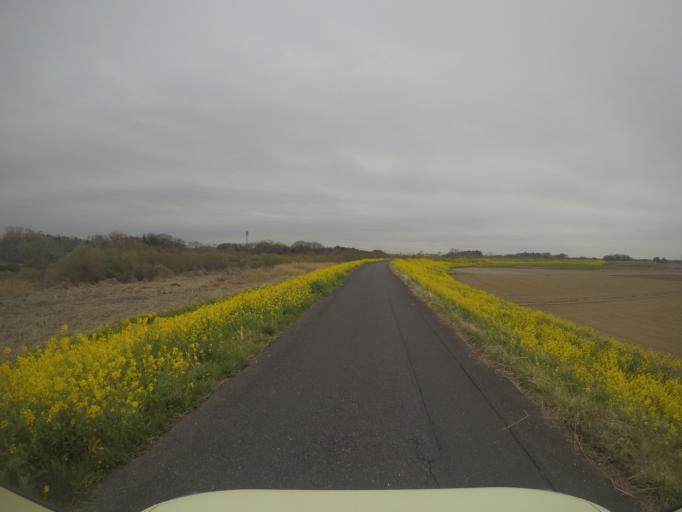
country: JP
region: Ibaraki
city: Ishige
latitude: 36.0977
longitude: 140.0044
